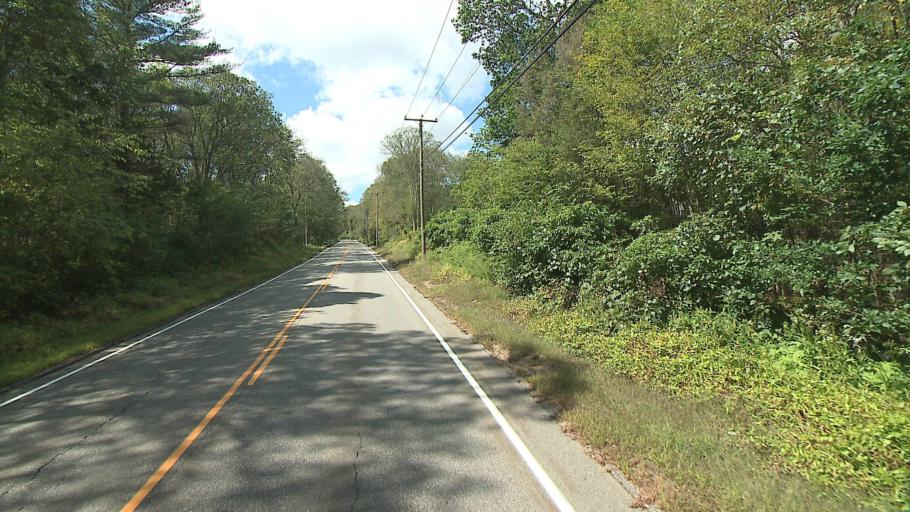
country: US
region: Connecticut
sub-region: Windham County
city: South Woodstock
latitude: 41.8793
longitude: -72.1038
